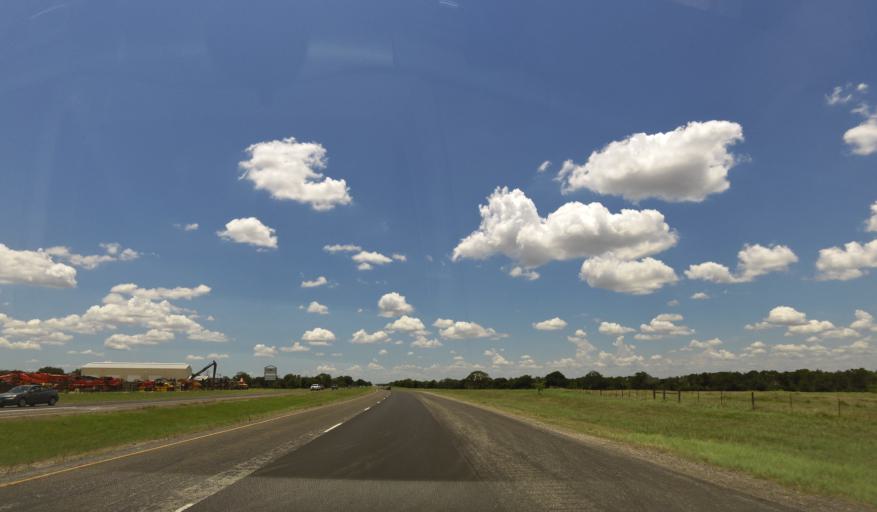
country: US
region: Texas
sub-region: Burleson County
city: Somerville
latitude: 30.1517
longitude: -96.6668
